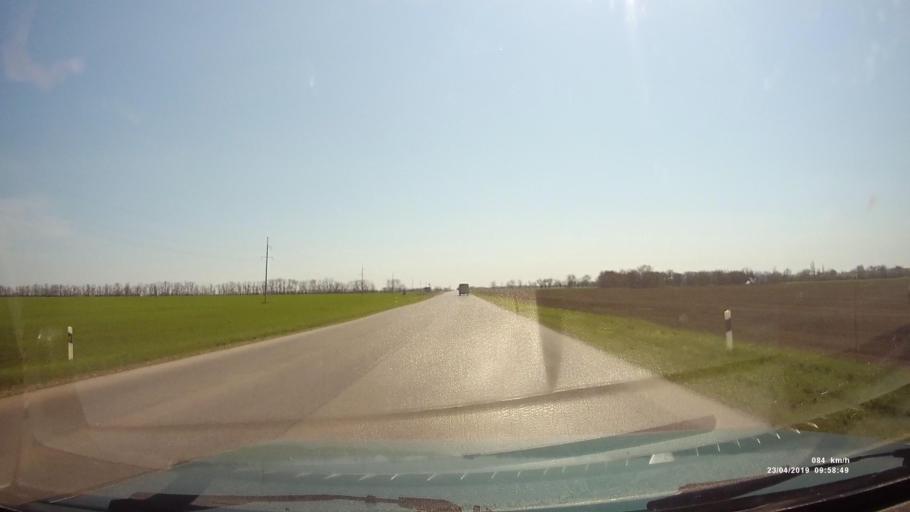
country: RU
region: Rostov
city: Sovetskoye
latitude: 46.7766
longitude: 42.1065
